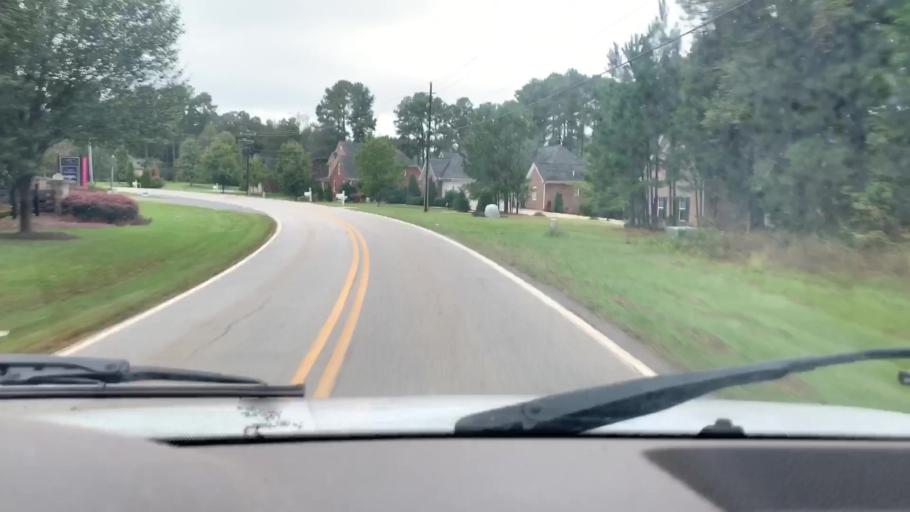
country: US
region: North Carolina
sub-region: Catawba County
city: Lake Norman of Catawba
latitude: 35.5616
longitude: -80.9095
